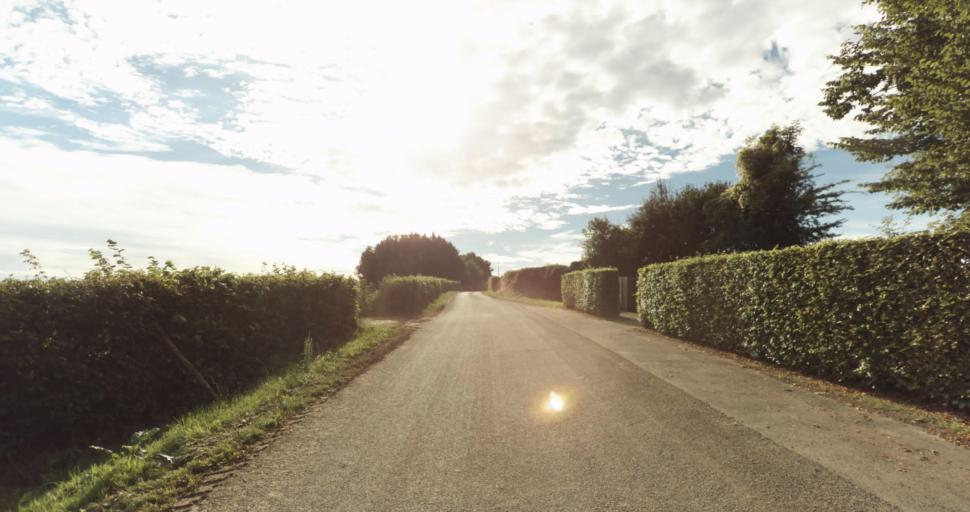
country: FR
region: Lower Normandy
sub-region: Departement de l'Orne
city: Vimoutiers
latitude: 48.8544
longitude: 0.2286
